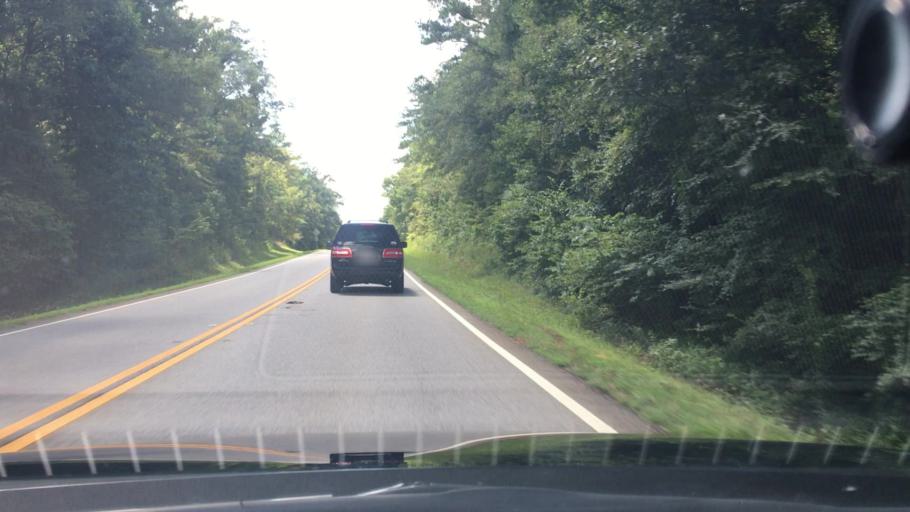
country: US
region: Georgia
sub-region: Jasper County
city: Monticello
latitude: 33.3119
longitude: -83.5367
